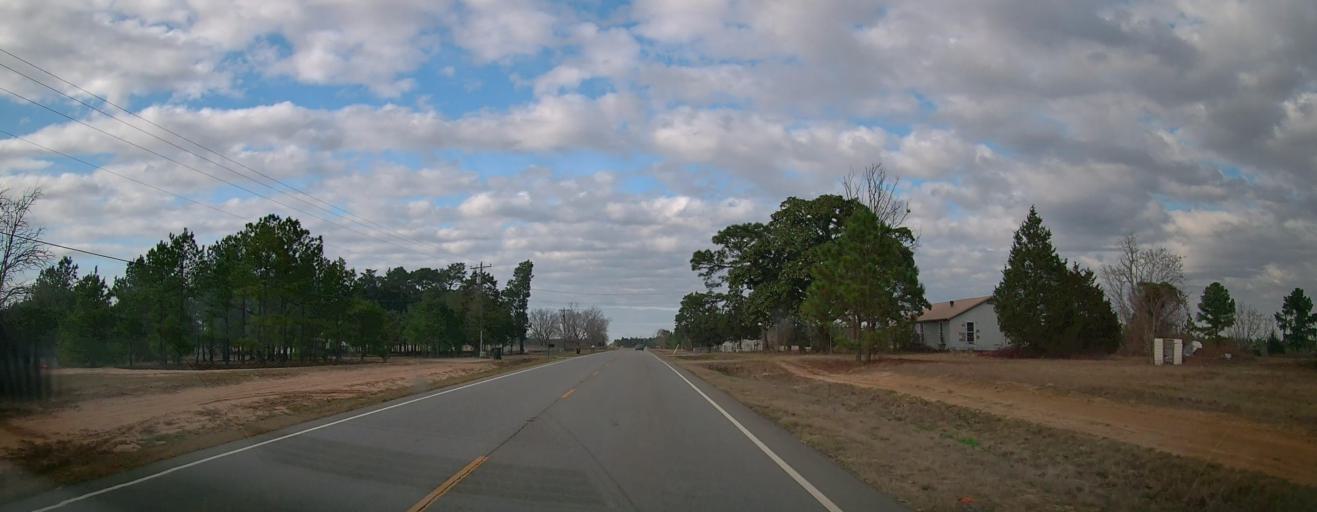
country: US
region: Georgia
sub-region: Marion County
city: Buena Vista
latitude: 32.4633
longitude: -84.5391
